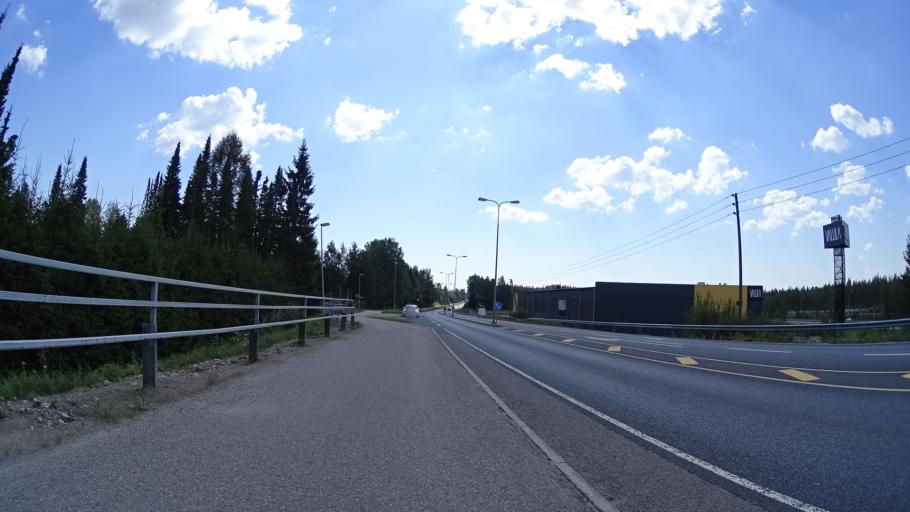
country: FI
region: Uusimaa
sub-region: Helsinki
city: Vantaa
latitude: 60.3406
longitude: 25.0039
